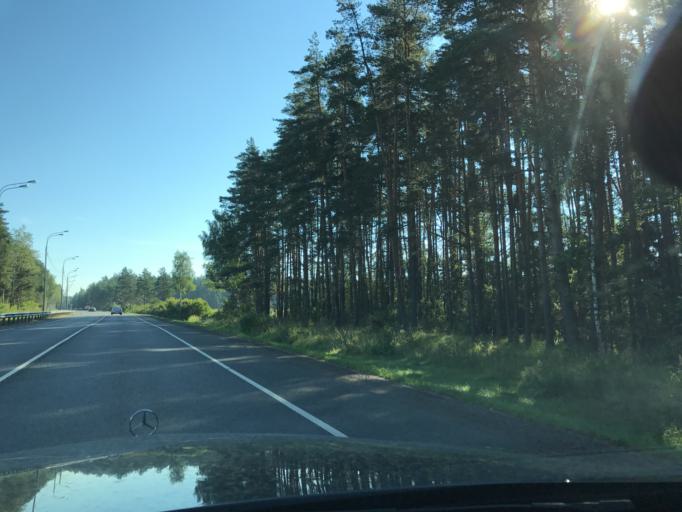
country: RU
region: Moskovskaya
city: Chernogolovka
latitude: 55.9651
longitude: 38.2825
